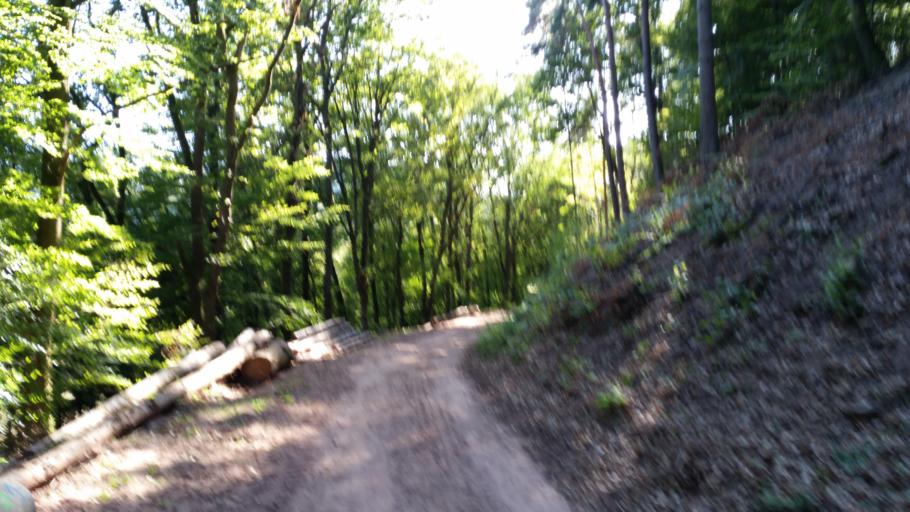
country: DE
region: Rheinland-Pfalz
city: Ludwigswinkel
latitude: 49.0380
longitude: 7.6870
